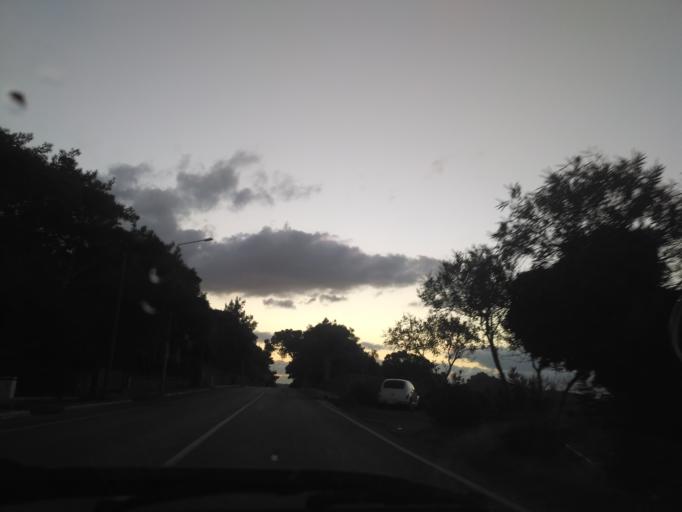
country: TR
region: Balikesir
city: Ayvalik
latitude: 39.3076
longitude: 26.6688
